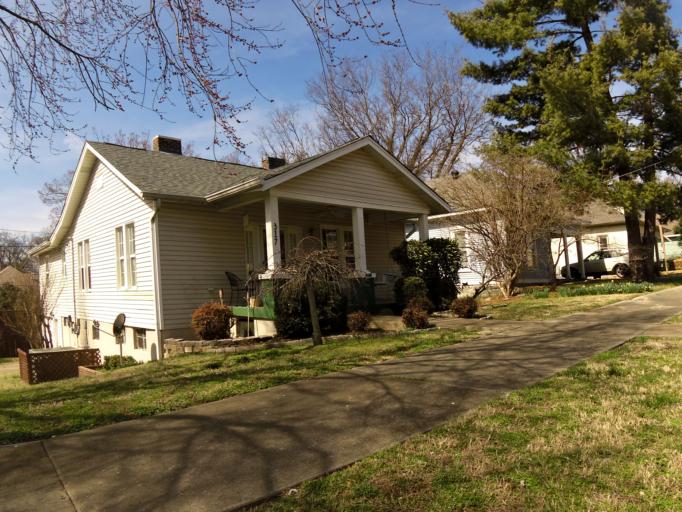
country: US
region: Tennessee
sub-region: Davidson County
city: Belle Meade
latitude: 36.1499
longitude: -86.8472
